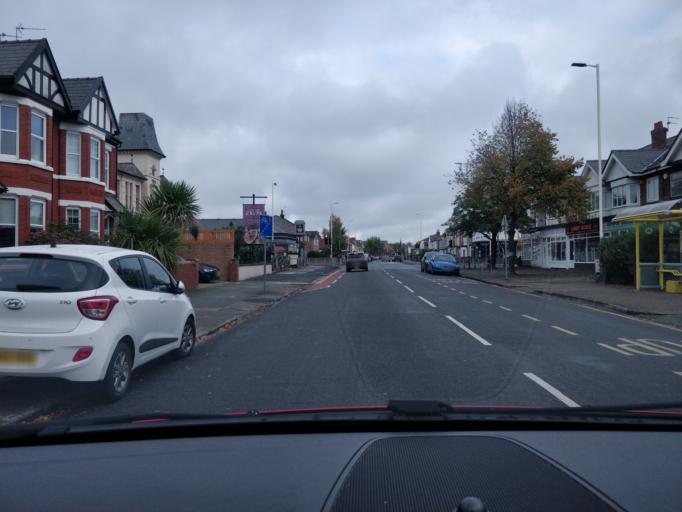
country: GB
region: England
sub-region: Sefton
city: Southport
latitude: 53.6171
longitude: -3.0163
